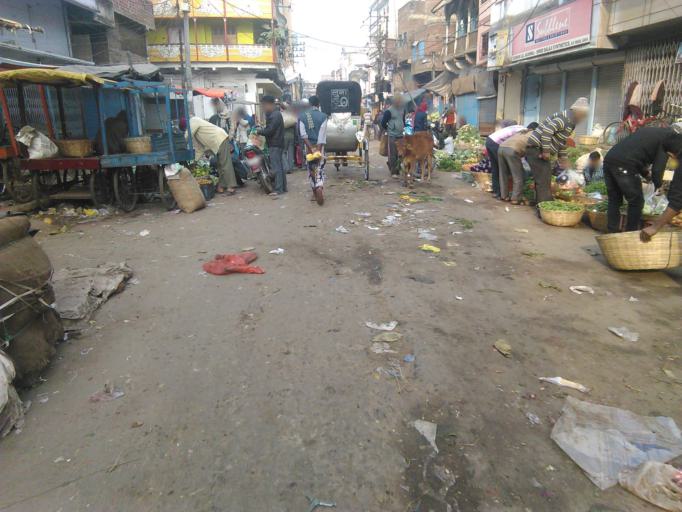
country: IN
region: Bihar
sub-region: Gaya
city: Gaya
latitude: 24.7977
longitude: 85.0052
